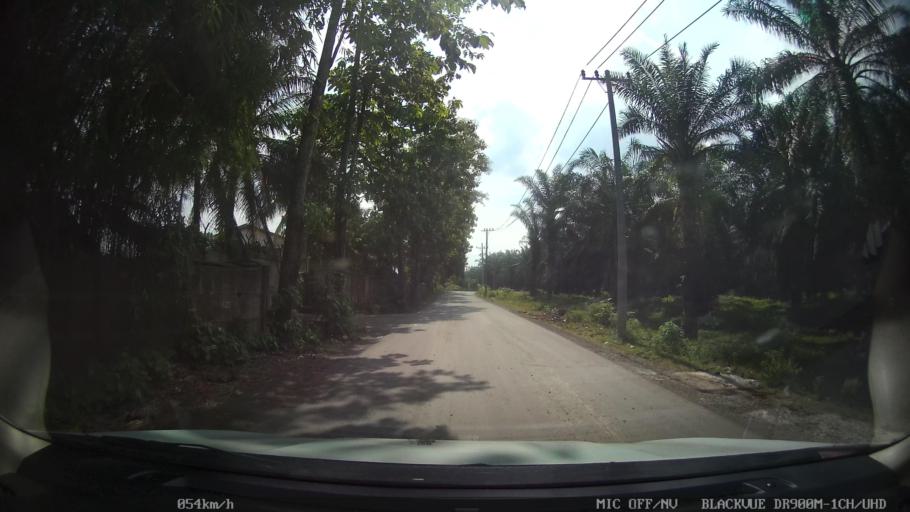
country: ID
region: North Sumatra
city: Binjai
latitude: 3.6353
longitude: 98.5330
